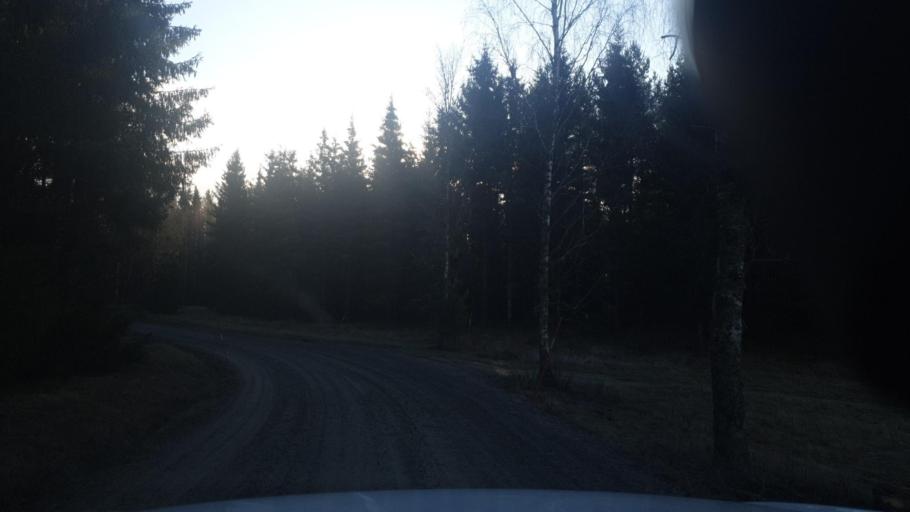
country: SE
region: Vaermland
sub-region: Sunne Kommun
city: Sunne
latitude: 59.6675
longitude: 13.0339
